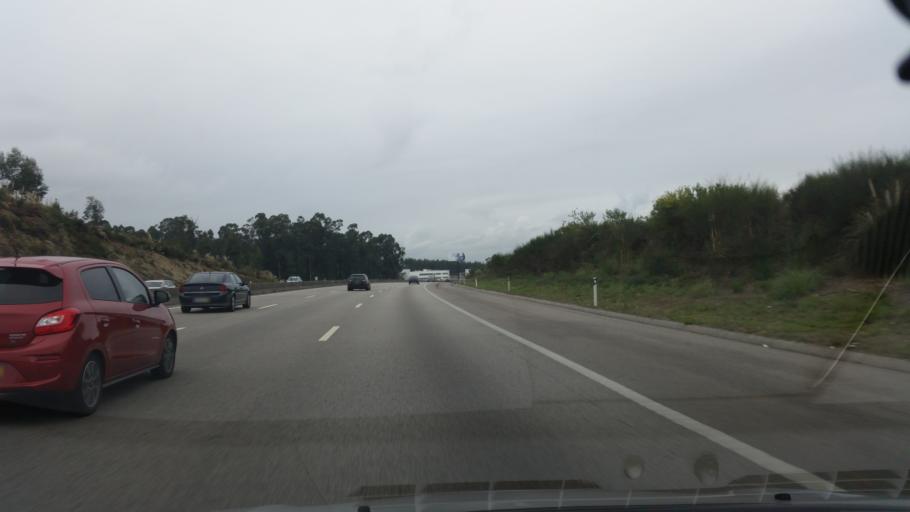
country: PT
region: Porto
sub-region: Maia
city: Nogueira
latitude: 41.2533
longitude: -8.5683
